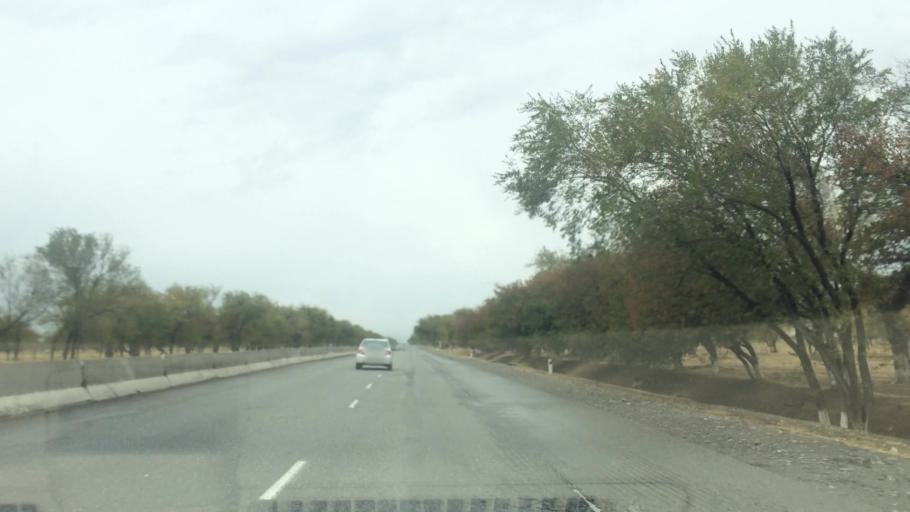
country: UZ
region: Samarqand
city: Bulung'ur
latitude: 39.8115
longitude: 67.3683
